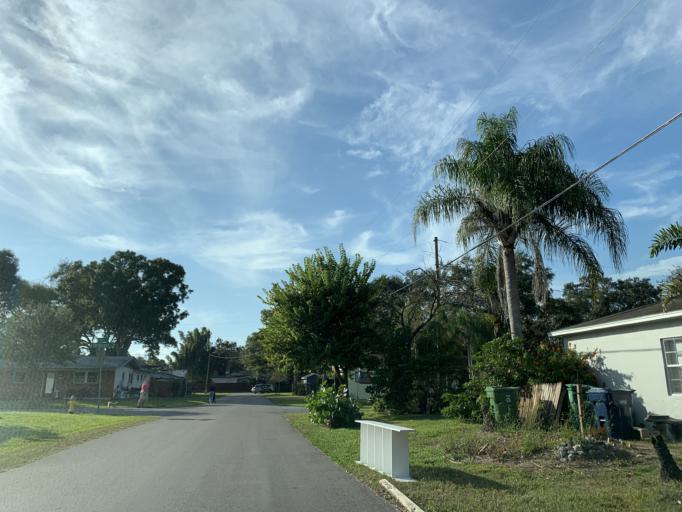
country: US
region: Florida
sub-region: Hillsborough County
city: Tampa
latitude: 27.8982
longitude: -82.4968
